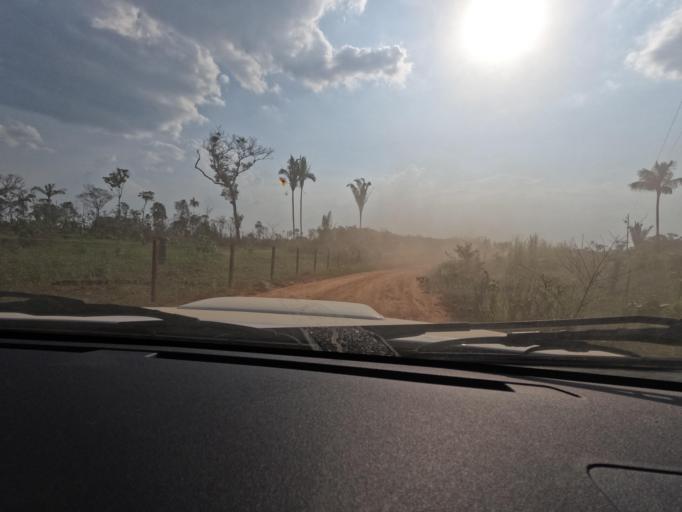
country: BR
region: Rondonia
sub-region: Porto Velho
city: Porto Velho
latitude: -8.5744
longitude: -64.0047
